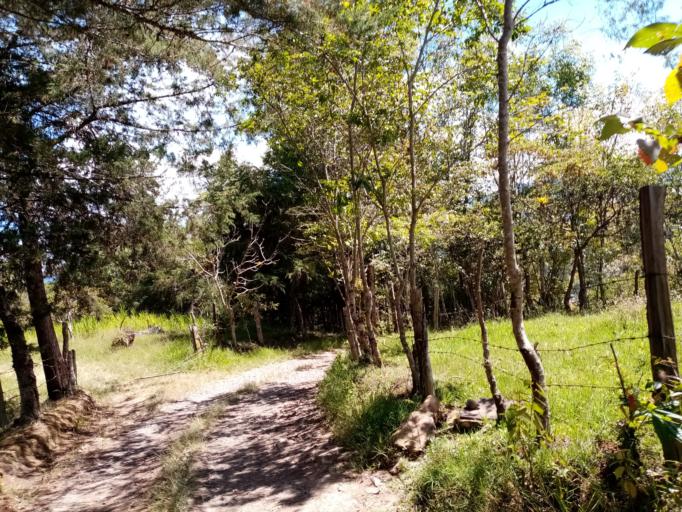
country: CO
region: Cundinamarca
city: Tenza
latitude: 5.0688
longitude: -73.4255
